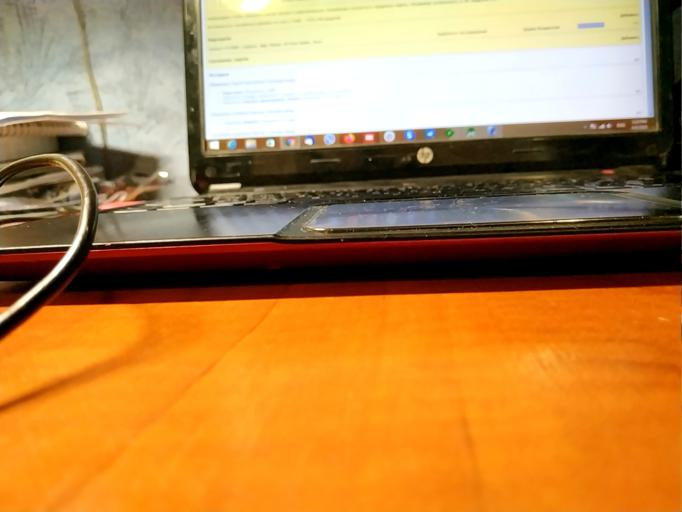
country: RU
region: Tverskaya
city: Sandovo
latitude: 58.6461
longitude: 36.4315
